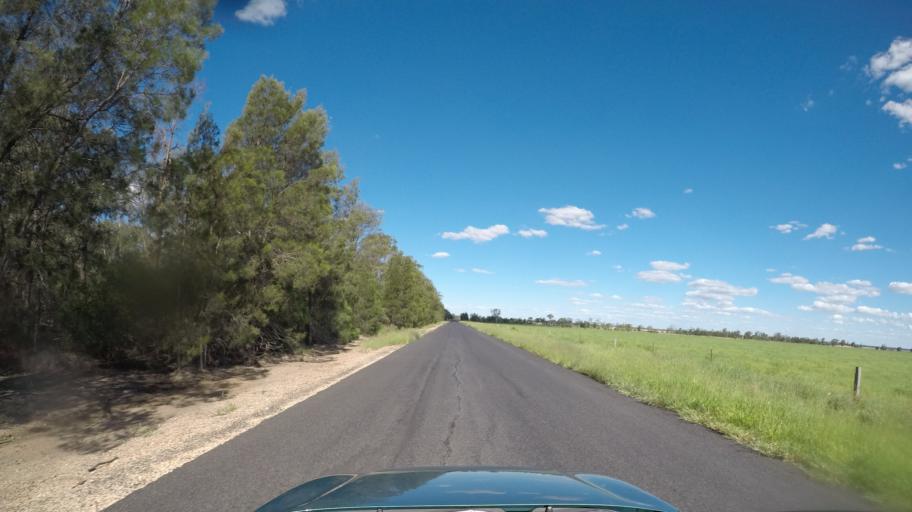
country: AU
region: Queensland
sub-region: Goondiwindi
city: Goondiwindi
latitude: -28.1553
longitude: 150.3703
